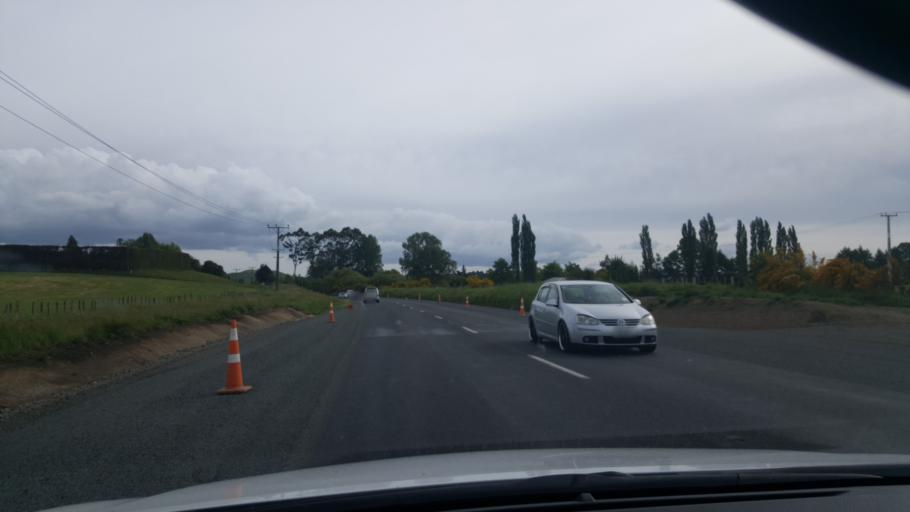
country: NZ
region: Bay of Plenty
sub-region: Rotorua District
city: Rotorua
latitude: -38.4122
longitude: 176.3210
